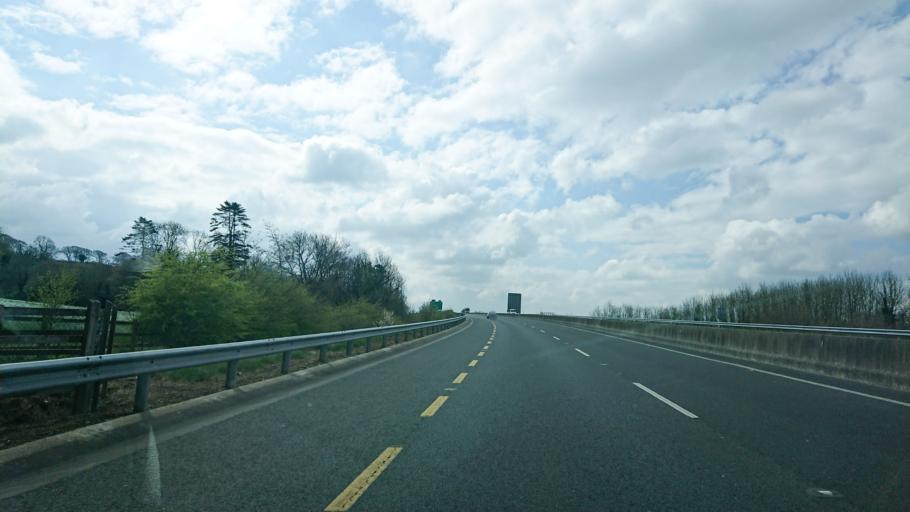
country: IE
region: Leinster
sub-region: Kilkenny
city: Mooncoin
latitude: 52.2540
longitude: -7.1898
